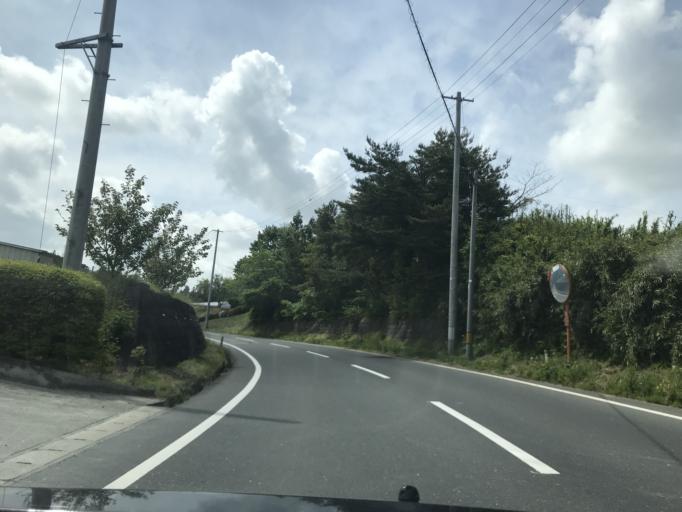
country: JP
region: Iwate
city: Ichinoseki
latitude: 38.7875
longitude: 141.0005
